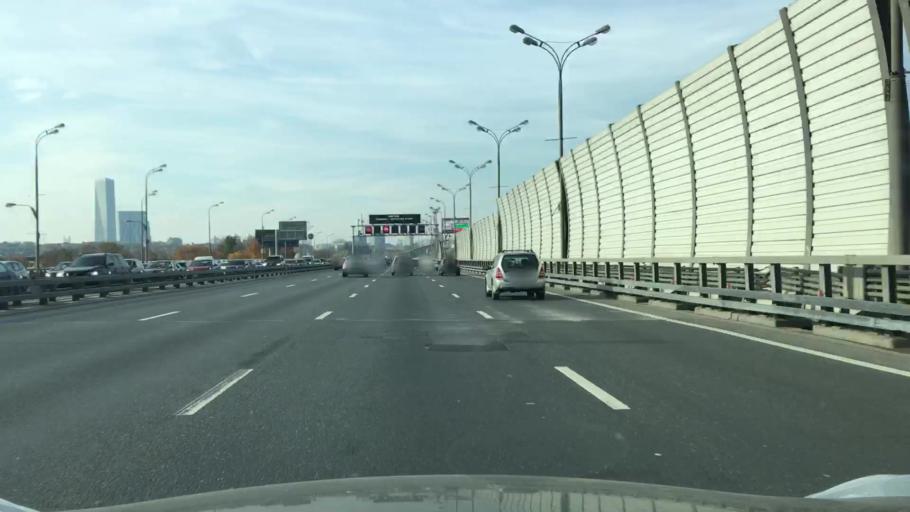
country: RU
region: Moscow
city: Luzhniki
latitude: 55.7208
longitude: 37.5626
